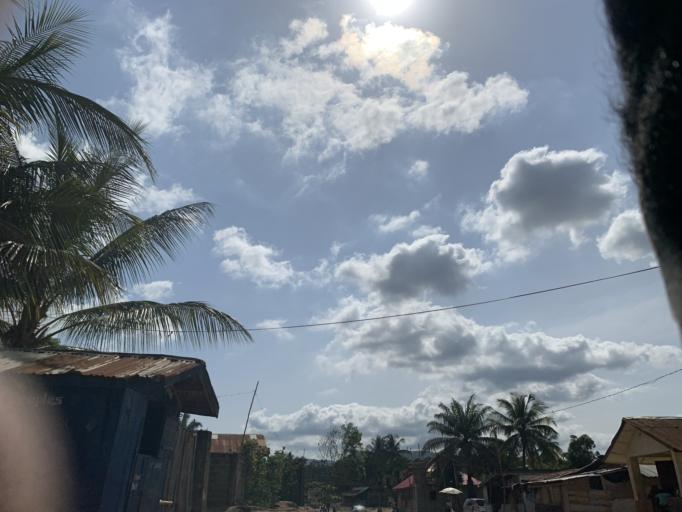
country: SL
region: Western Area
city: Waterloo
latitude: 8.3302
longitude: -13.0539
